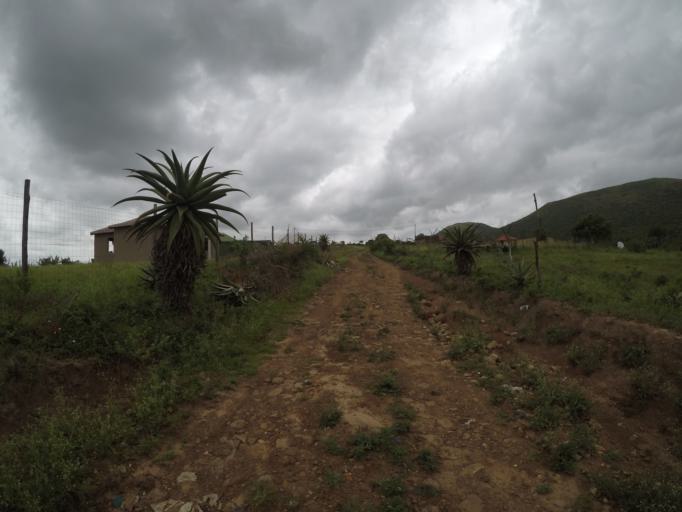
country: ZA
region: KwaZulu-Natal
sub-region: uThungulu District Municipality
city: Empangeni
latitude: -28.5822
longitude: 31.8673
